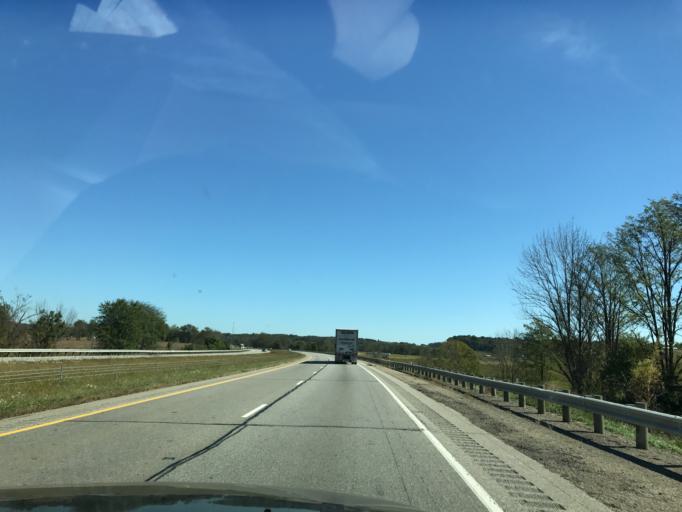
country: US
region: Ohio
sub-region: Perry County
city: Somerset
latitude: 39.9360
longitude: -82.2488
